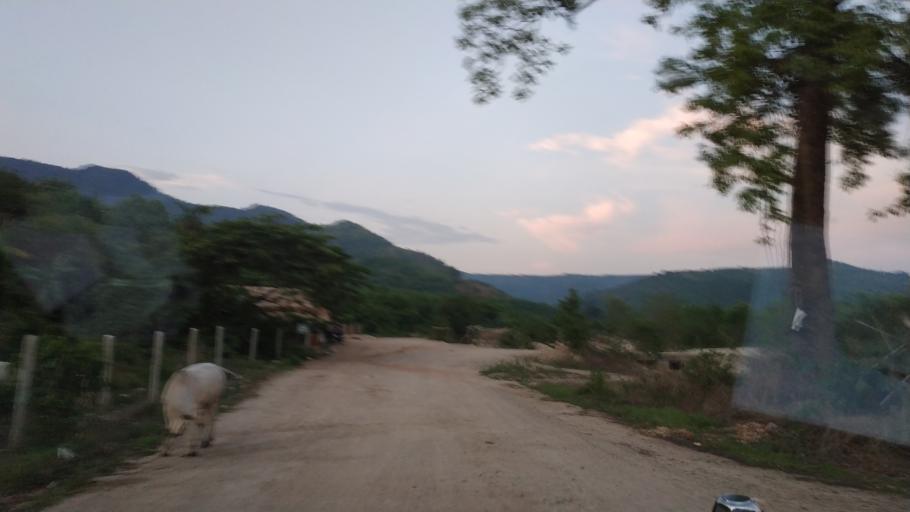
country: MM
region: Mon
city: Kyaikto
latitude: 17.4167
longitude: 97.0584
